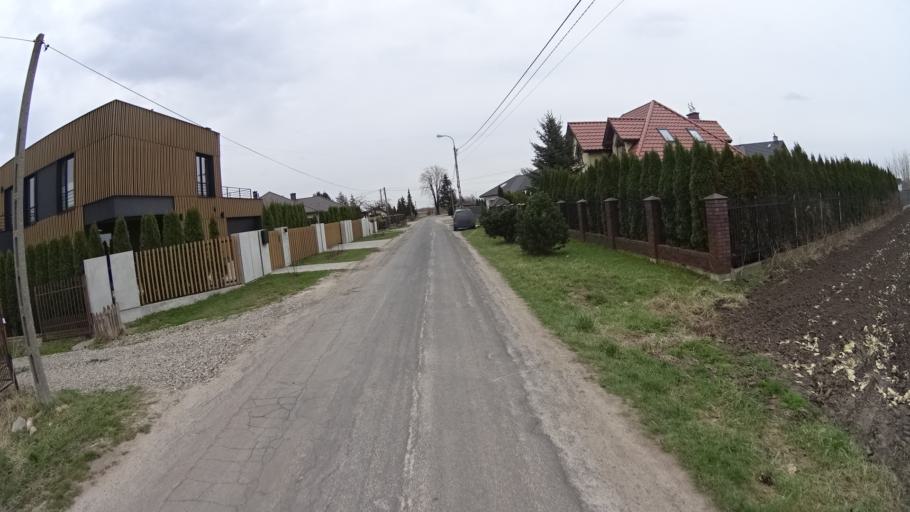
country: PL
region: Masovian Voivodeship
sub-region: Powiat warszawski zachodni
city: Ozarow Mazowiecki
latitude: 52.2449
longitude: 20.7537
